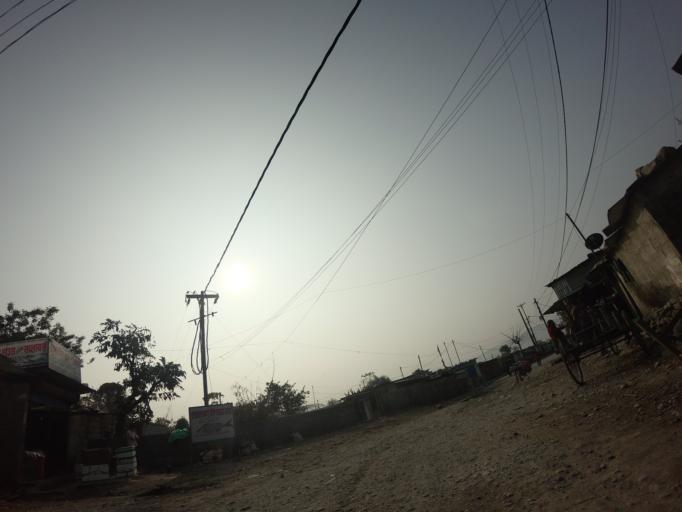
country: NP
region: Western Region
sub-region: Gandaki Zone
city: Pokhara
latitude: 28.2077
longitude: 83.9892
